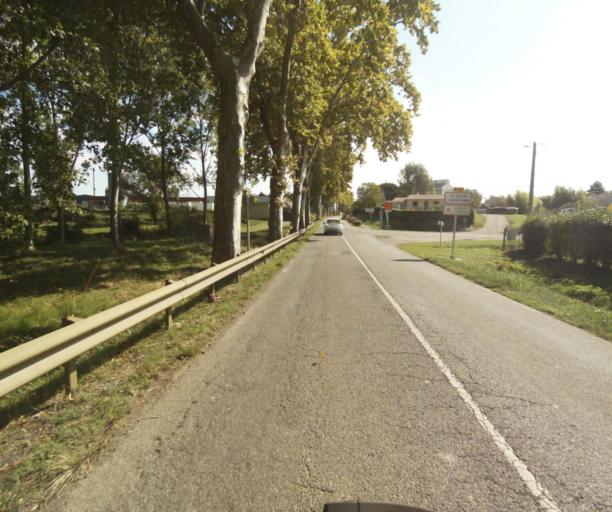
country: FR
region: Midi-Pyrenees
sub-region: Departement du Tarn-et-Garonne
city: Verdun-sur-Garonne
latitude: 43.8556
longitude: 1.2217
